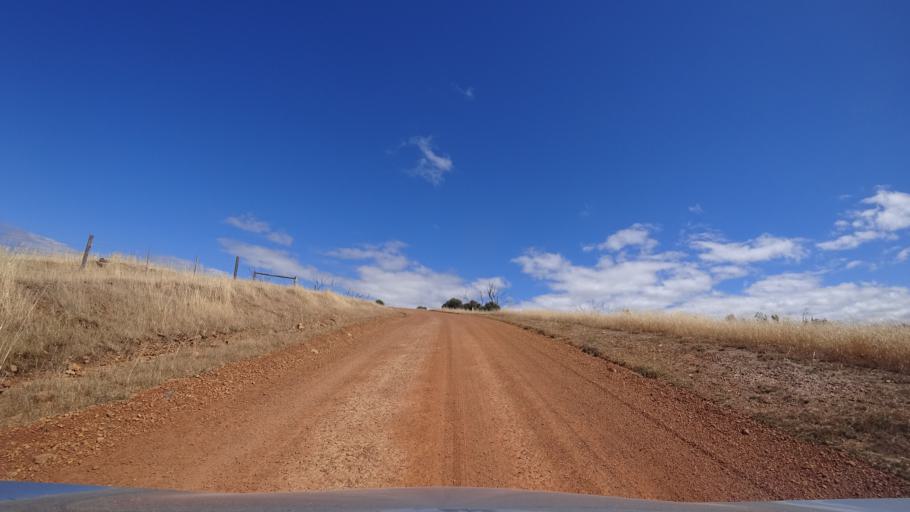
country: AU
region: South Australia
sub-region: Kangaroo Island
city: Kingscote
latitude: -35.6871
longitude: 136.9762
